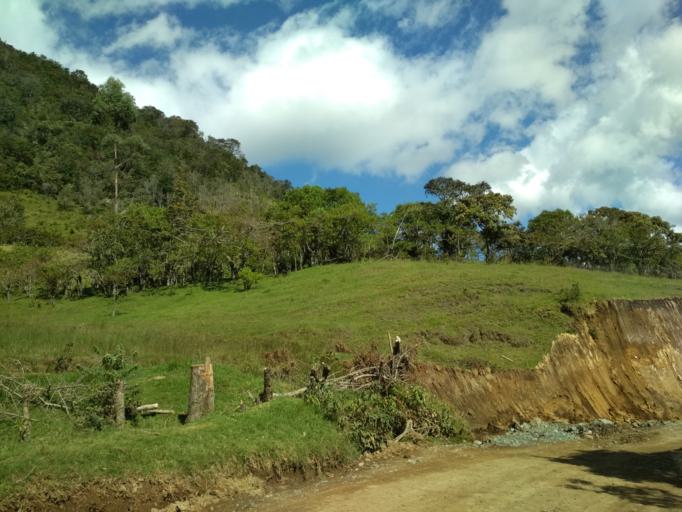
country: CO
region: Cauca
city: Jambalo
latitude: 2.7056
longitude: -76.3288
